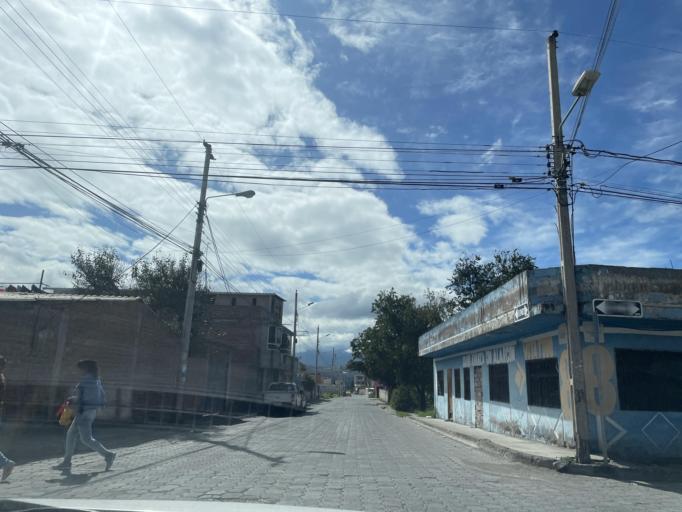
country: EC
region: Chimborazo
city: Guano
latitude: -1.6071
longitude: -78.6334
